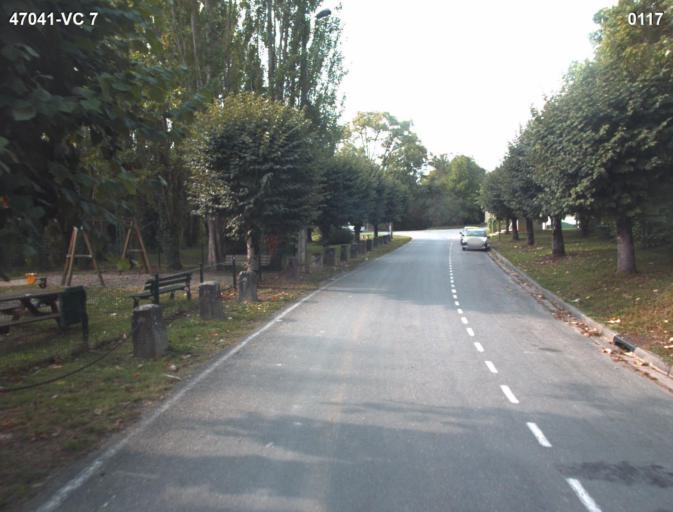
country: FR
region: Aquitaine
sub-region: Departement du Lot-et-Garonne
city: Port-Sainte-Marie
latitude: 44.2044
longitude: 0.4130
